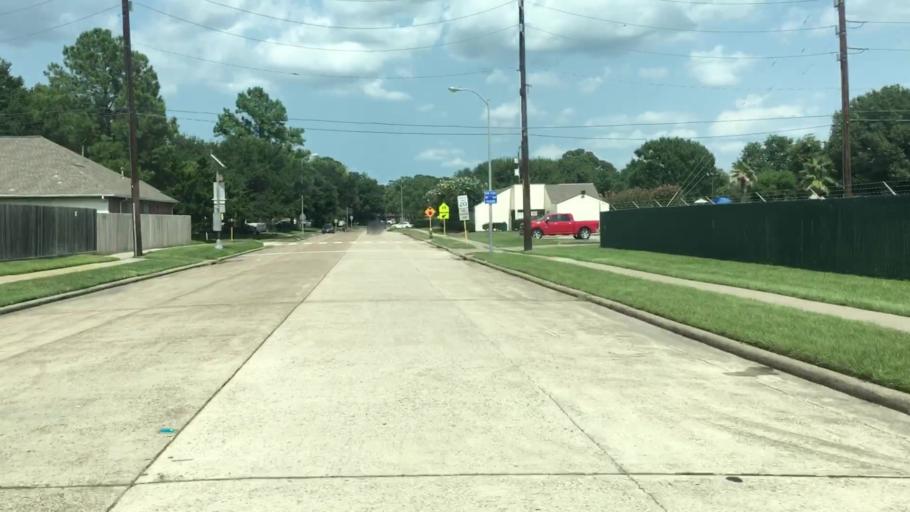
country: US
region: Texas
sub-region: Harris County
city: Atascocita
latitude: 29.9919
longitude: -95.1706
